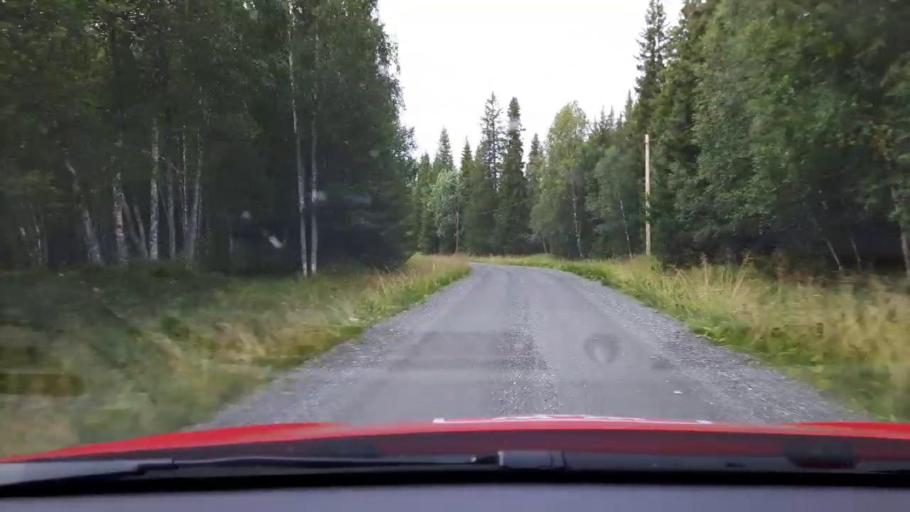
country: SE
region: Jaemtland
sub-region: Are Kommun
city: Are
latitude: 63.7724
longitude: 13.0807
